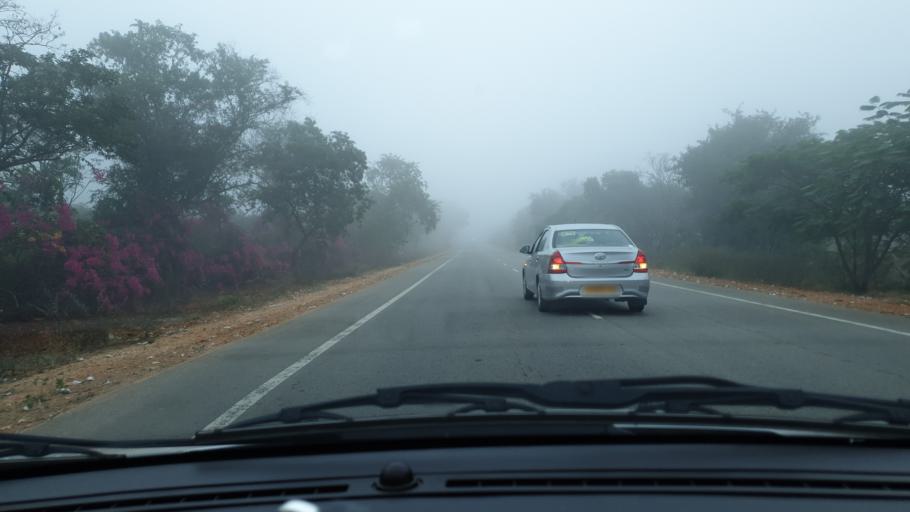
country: IN
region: Telangana
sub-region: Mahbubnagar
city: Nagar Karnul
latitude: 16.6425
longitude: 78.5898
